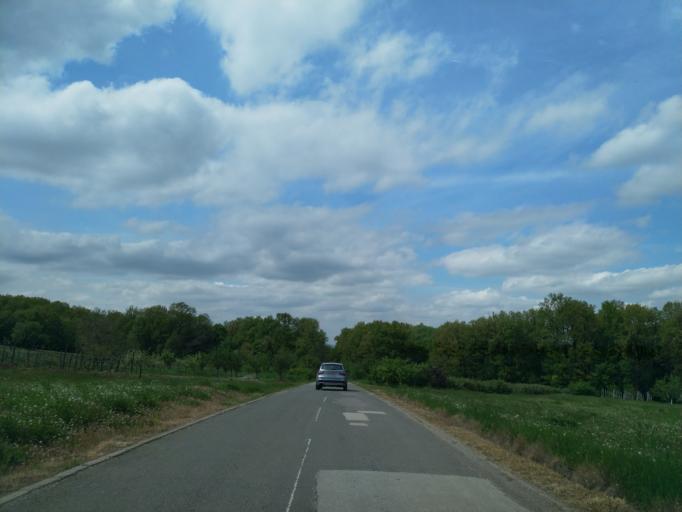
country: RS
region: Central Serbia
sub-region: Pomoravski Okrug
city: Paracin
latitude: 43.9476
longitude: 21.4923
